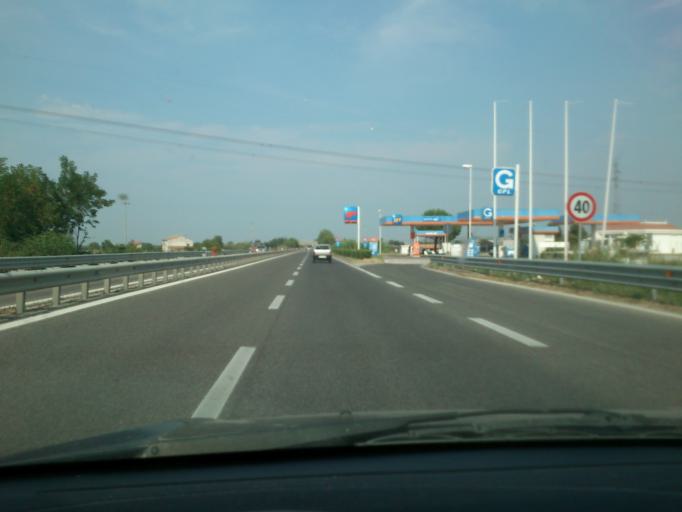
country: IT
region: The Marches
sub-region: Provincia di Pesaro e Urbino
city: Cuccurano
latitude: 43.7748
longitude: 12.9729
